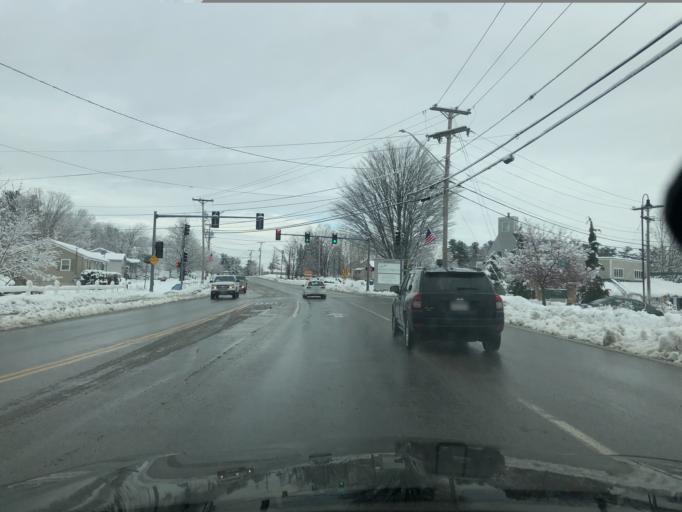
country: US
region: New Hampshire
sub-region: Strafford County
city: Somersworth
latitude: 43.2392
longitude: -70.8790
